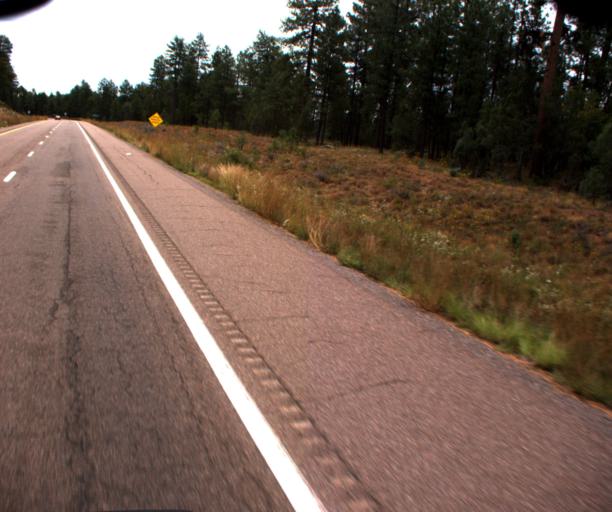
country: US
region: Arizona
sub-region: Gila County
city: Star Valley
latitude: 34.2956
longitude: -110.9828
